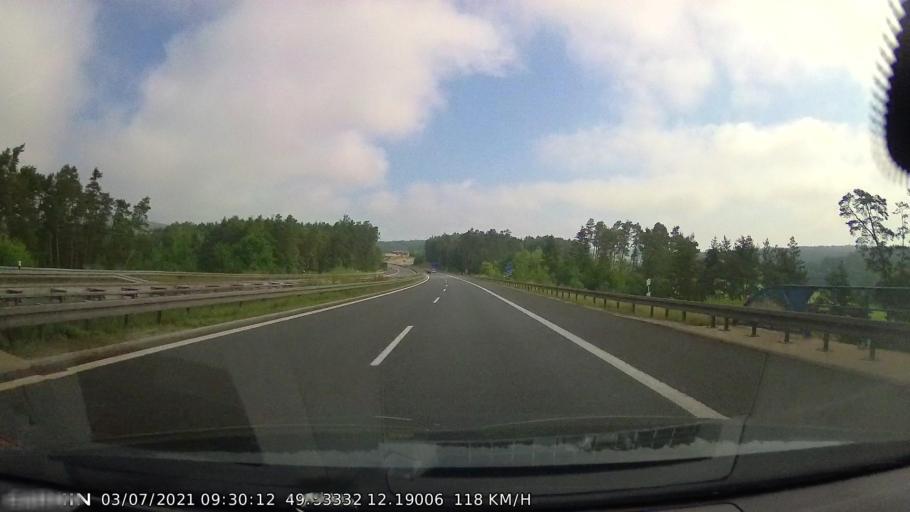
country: DE
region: Bavaria
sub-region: Upper Palatinate
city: Wernberg-Koblitz
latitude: 49.5335
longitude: 12.1902
